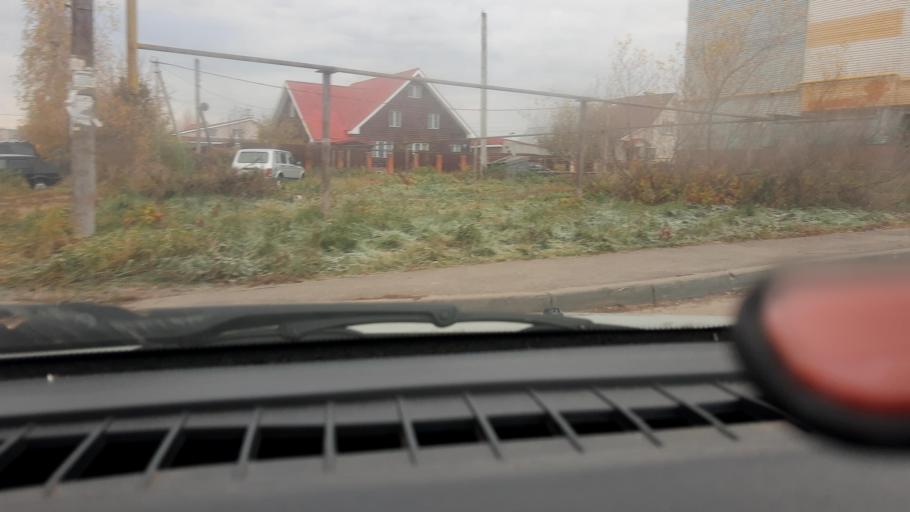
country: RU
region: Nizjnij Novgorod
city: Afonino
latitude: 56.2098
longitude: 44.0973
